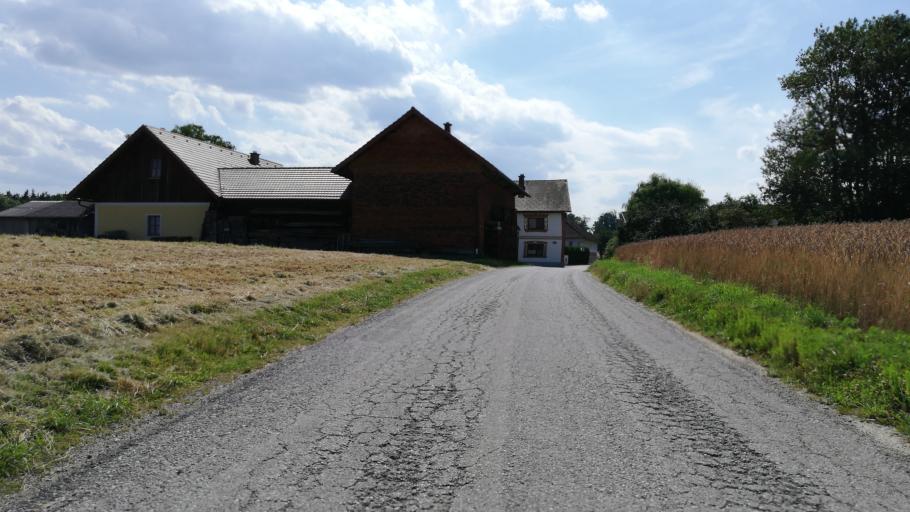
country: AT
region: Upper Austria
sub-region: Wels-Land
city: Edt bei Lambach
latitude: 48.1664
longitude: 13.8882
